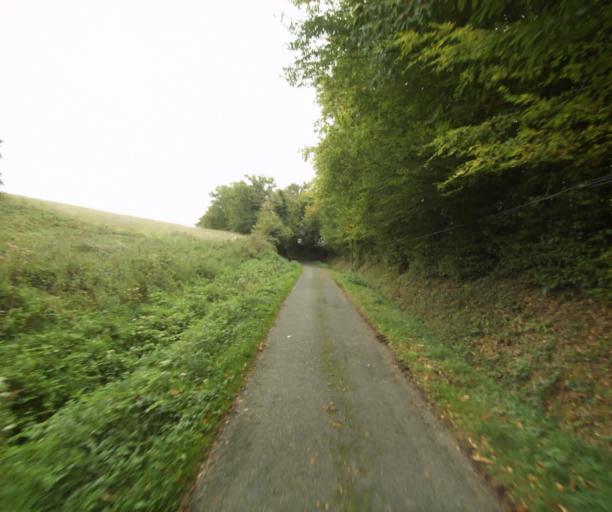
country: FR
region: Midi-Pyrenees
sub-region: Departement du Gers
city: Eauze
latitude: 43.8953
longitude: 0.0629
